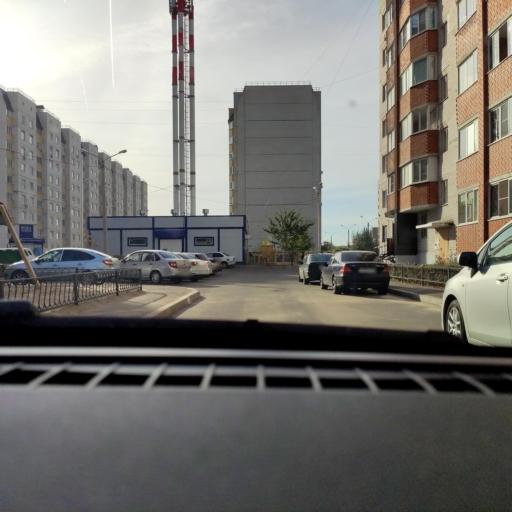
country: RU
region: Voronezj
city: Somovo
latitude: 51.7409
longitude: 39.3116
